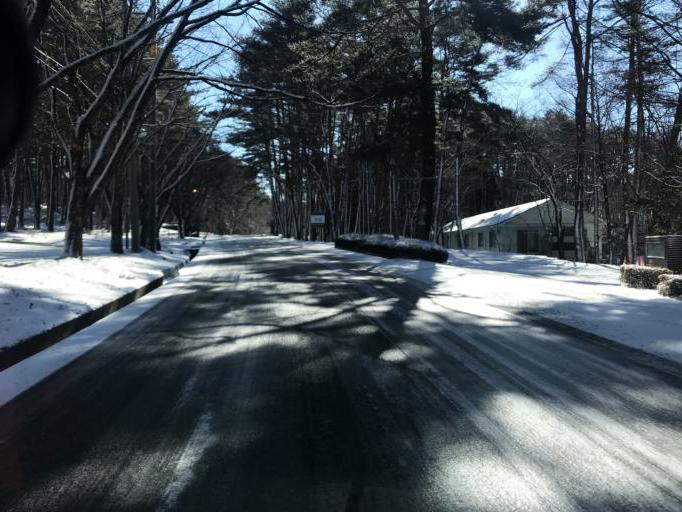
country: JP
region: Nagano
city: Chino
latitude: 35.8777
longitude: 138.3181
